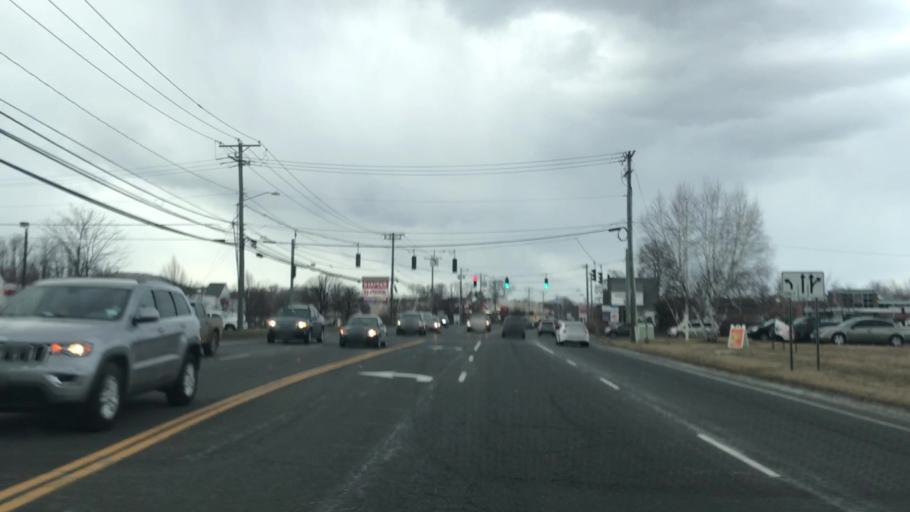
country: US
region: Connecticut
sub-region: Litchfield County
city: New Milford
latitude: 41.5557
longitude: -73.4173
